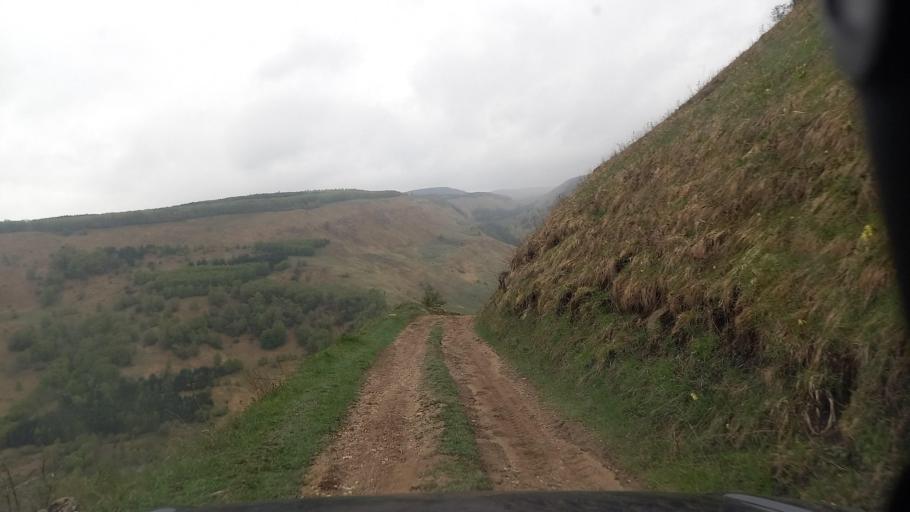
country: RU
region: Stavropol'skiy
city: Nezhinskiy
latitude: 43.8535
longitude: 42.6386
